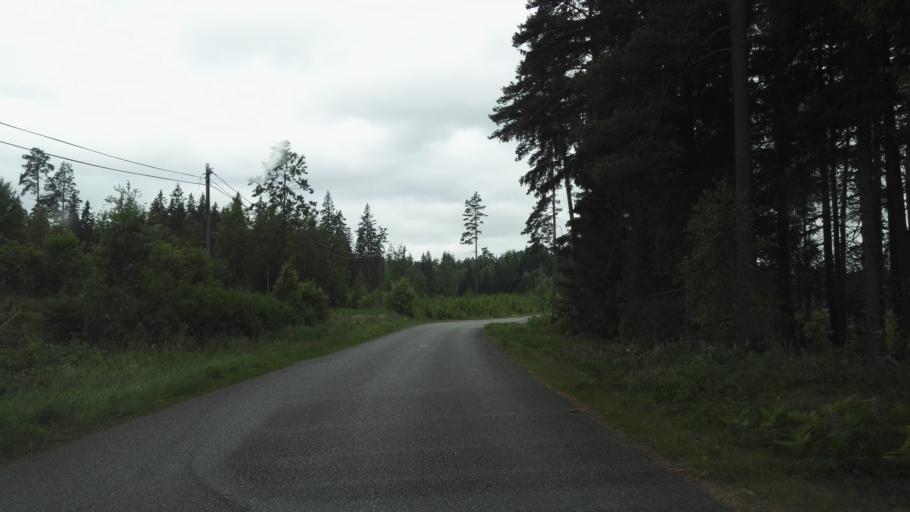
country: SE
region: Joenkoeping
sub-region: Vetlanda Kommun
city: Landsbro
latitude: 57.2961
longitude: 14.8478
